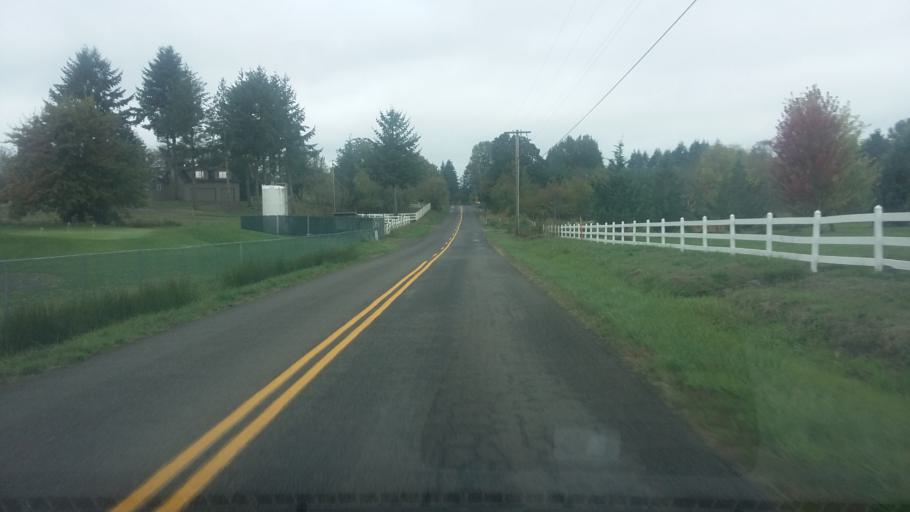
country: US
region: Washington
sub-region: Clark County
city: La Center
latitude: 45.8374
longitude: -122.6901
